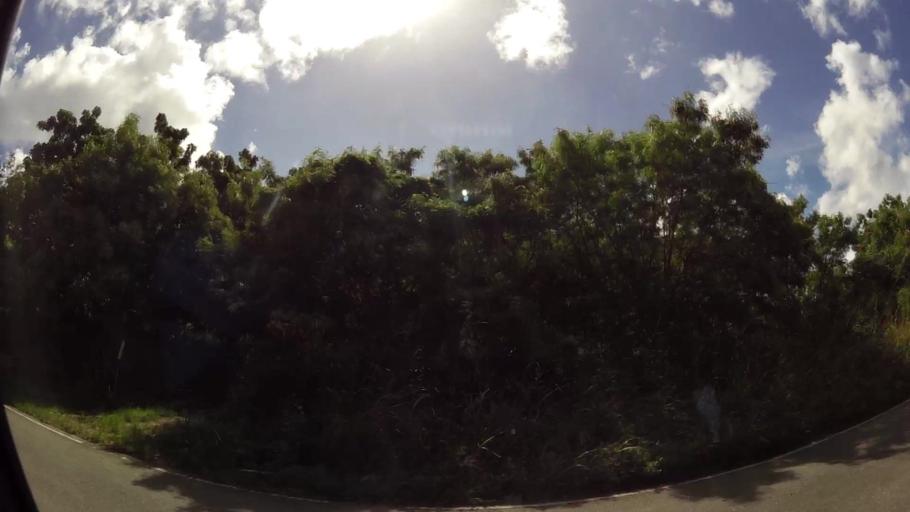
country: BB
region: Saint James
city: Holetown
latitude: 13.1936
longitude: -59.6282
